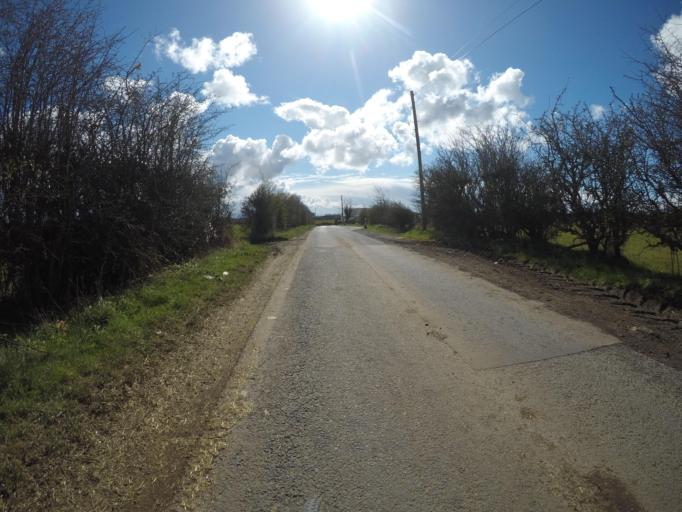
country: GB
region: Scotland
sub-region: North Ayrshire
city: Kilwinning
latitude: 55.6692
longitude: -4.7200
